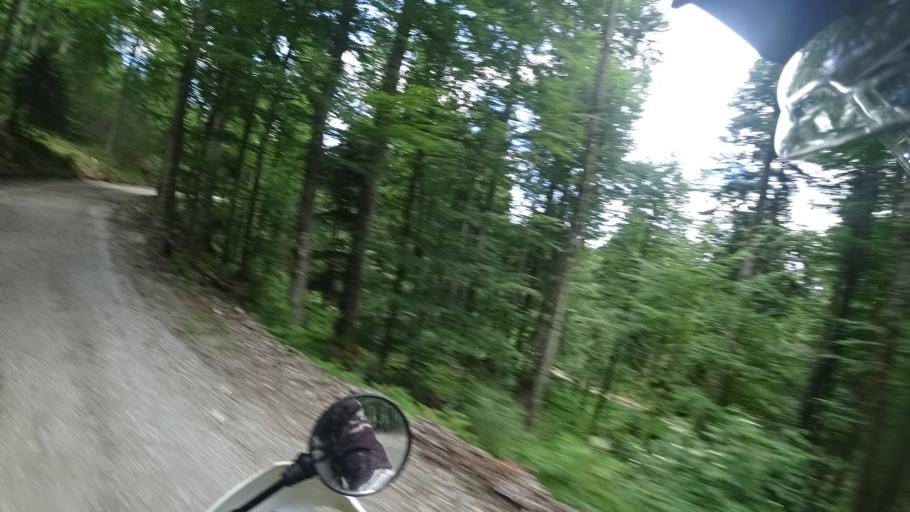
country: SI
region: Osilnica
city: Osilnica
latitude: 45.5110
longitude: 14.6126
